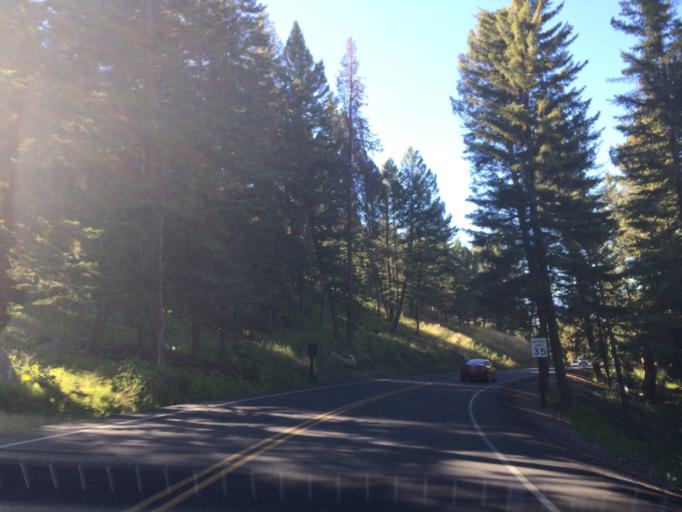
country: US
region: Montana
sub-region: Gallatin County
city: West Yellowstone
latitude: 44.9023
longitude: -110.3969
